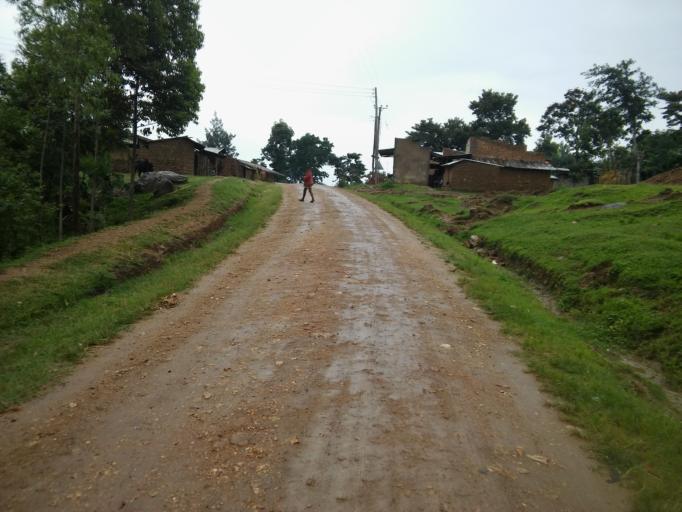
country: UG
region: Eastern Region
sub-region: Mbale District
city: Mbale
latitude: 1.0175
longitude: 34.2215
